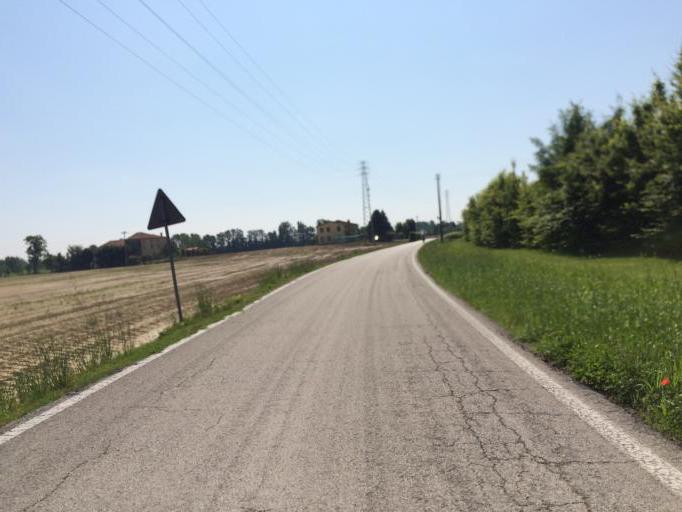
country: IT
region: Veneto
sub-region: Provincia di Vicenza
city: Montegalda
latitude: 45.4725
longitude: 11.6733
